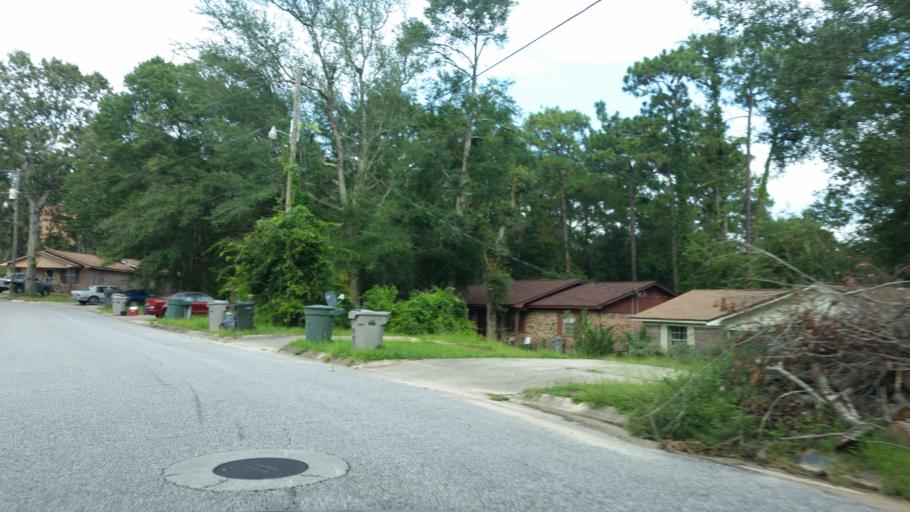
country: US
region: Florida
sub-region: Escambia County
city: Ferry Pass
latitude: 30.5129
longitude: -87.1712
